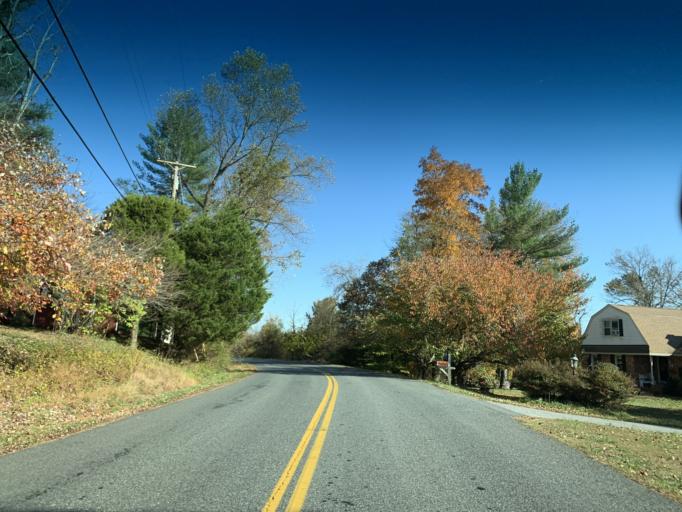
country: US
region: Maryland
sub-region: Harford County
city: Joppatowne
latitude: 39.4724
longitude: -76.3620
